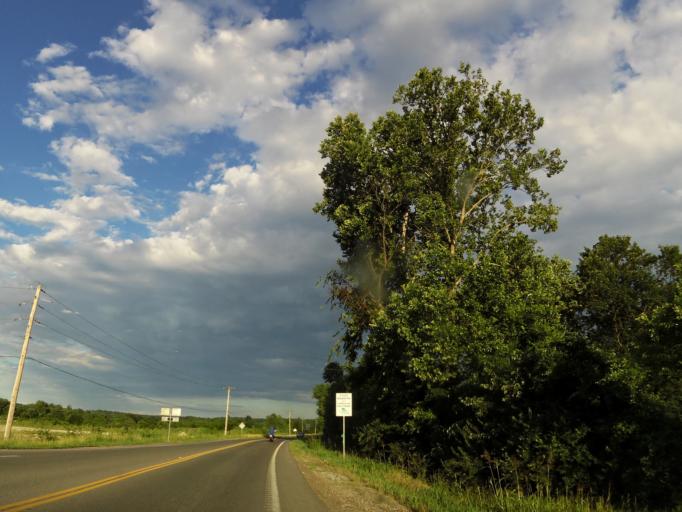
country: US
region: Missouri
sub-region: Saint Louis County
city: Eureka
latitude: 38.4771
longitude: -90.6373
